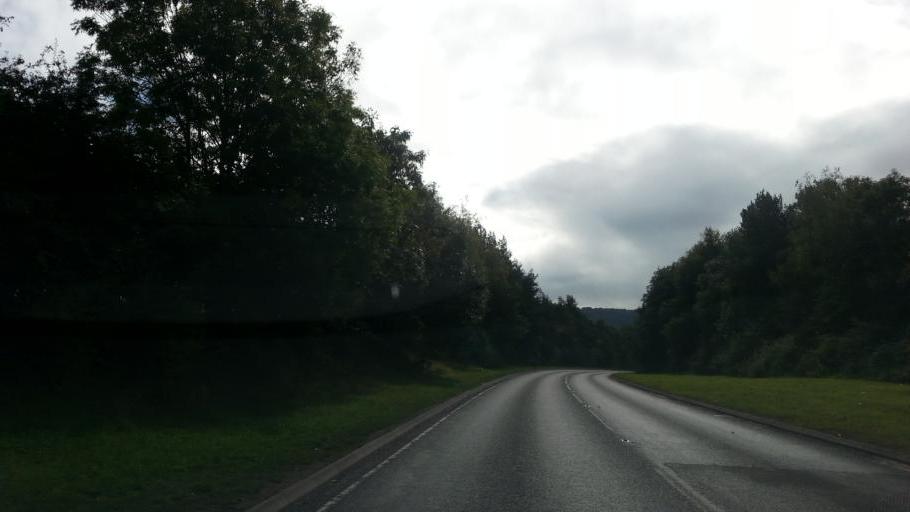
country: GB
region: England
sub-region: Herefordshire
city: Ross on Wye
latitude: 51.9265
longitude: -2.5719
